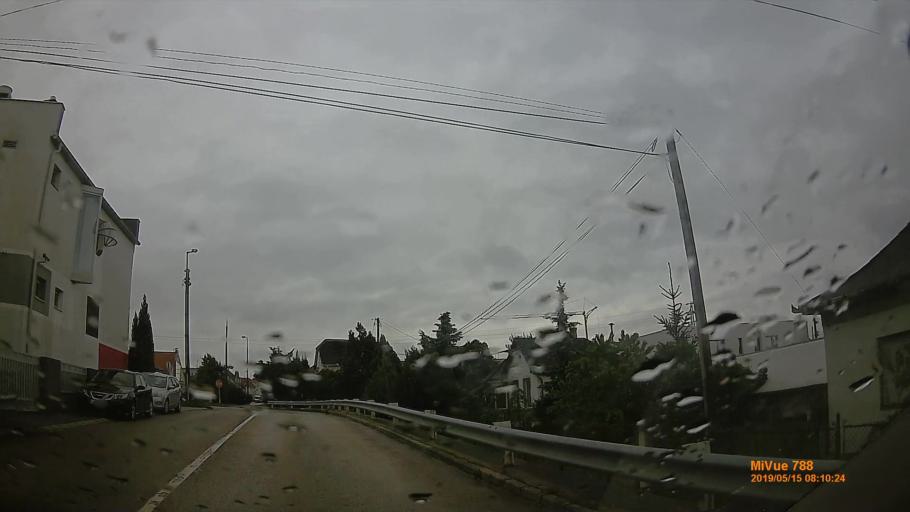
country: HU
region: Veszprem
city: Veszprem
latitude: 47.0976
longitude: 17.9221
